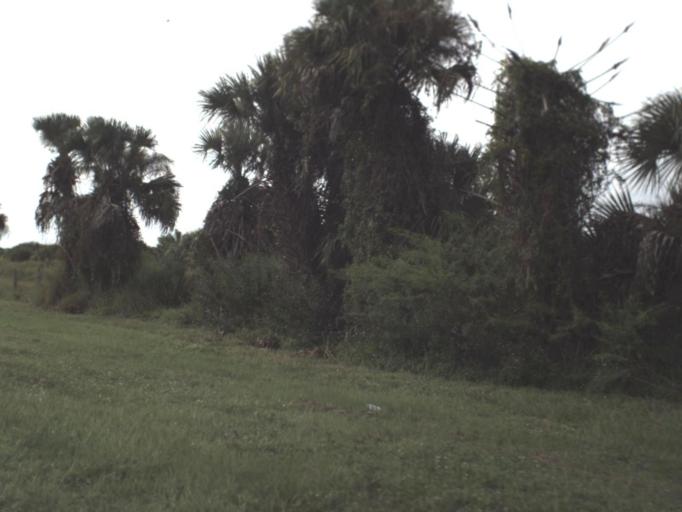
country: US
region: Florida
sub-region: Hendry County
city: Port LaBelle
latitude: 26.7685
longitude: -81.2826
